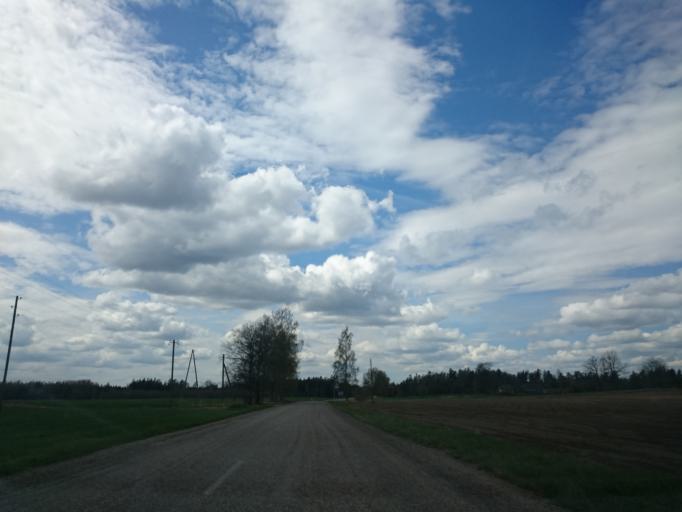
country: LV
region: Talsu Rajons
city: Sabile
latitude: 56.9516
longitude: 22.3111
